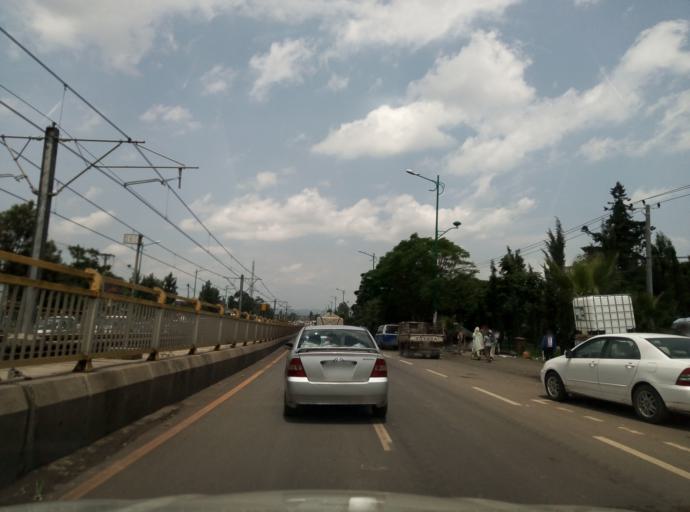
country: ET
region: Adis Abeba
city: Addis Ababa
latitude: 8.9508
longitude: 38.7635
